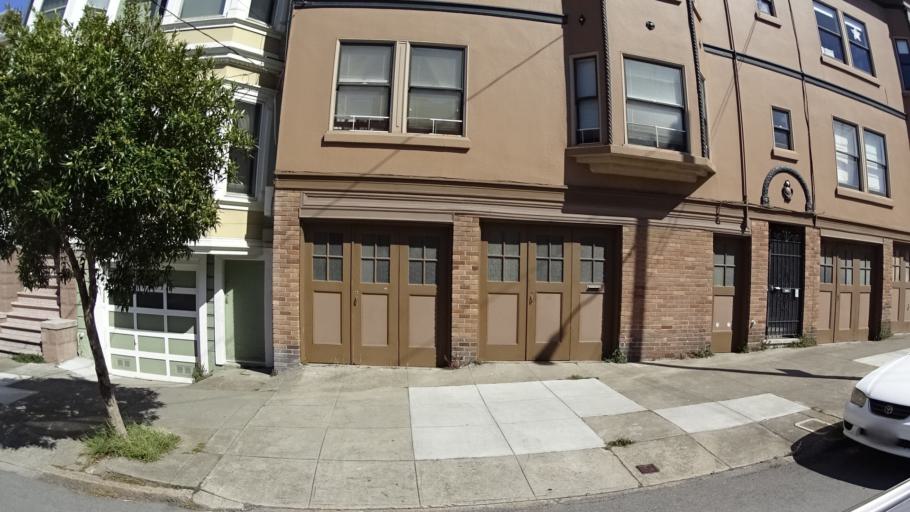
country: US
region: California
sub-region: San Francisco County
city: San Francisco
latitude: 37.7624
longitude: -122.4683
